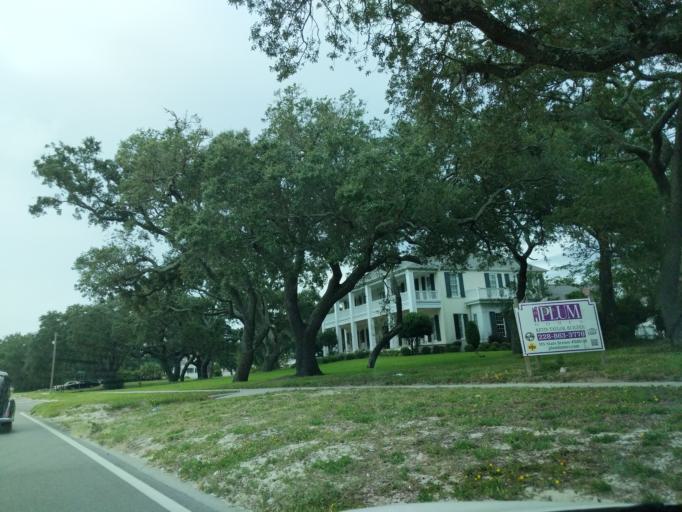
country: US
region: Mississippi
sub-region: Harrison County
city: Gulfport
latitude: 30.3750
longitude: -89.0616
